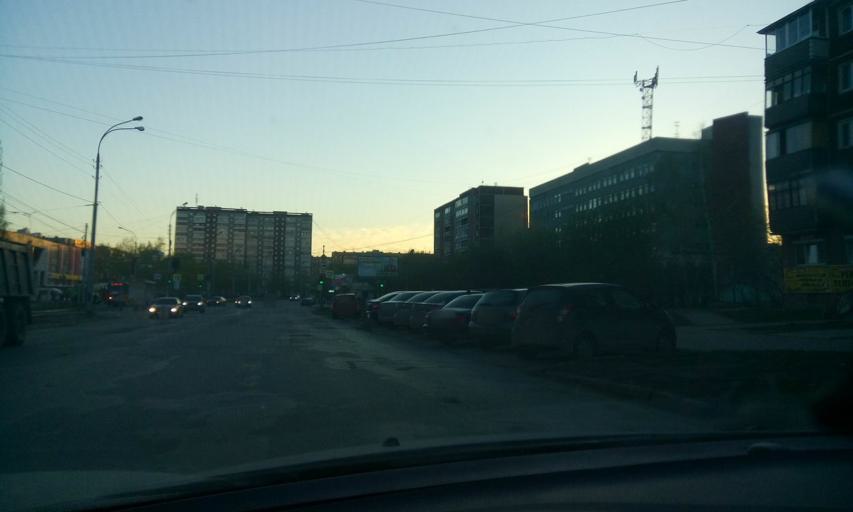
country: RU
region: Sverdlovsk
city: Yekaterinburg
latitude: 56.8352
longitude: 60.6864
